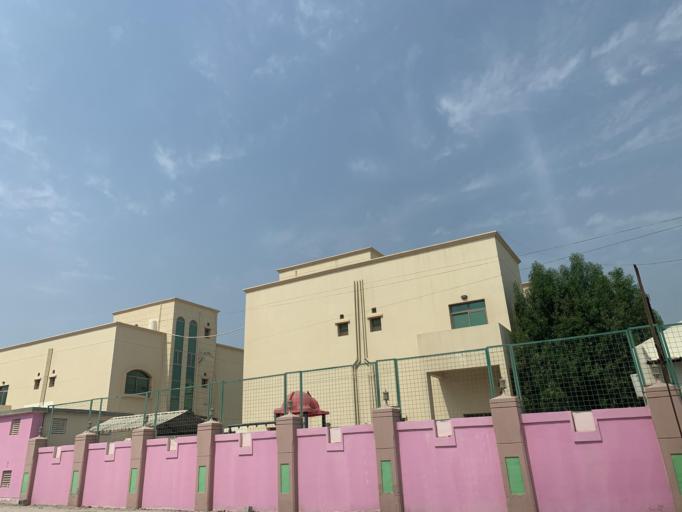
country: BH
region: Manama
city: Jidd Hafs
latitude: 26.2163
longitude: 50.4872
